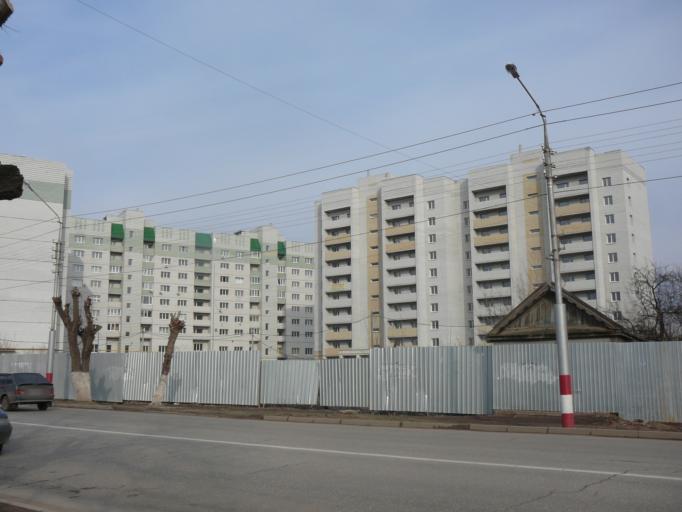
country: RU
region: Saratov
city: Engel's
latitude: 51.4881
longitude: 46.1207
